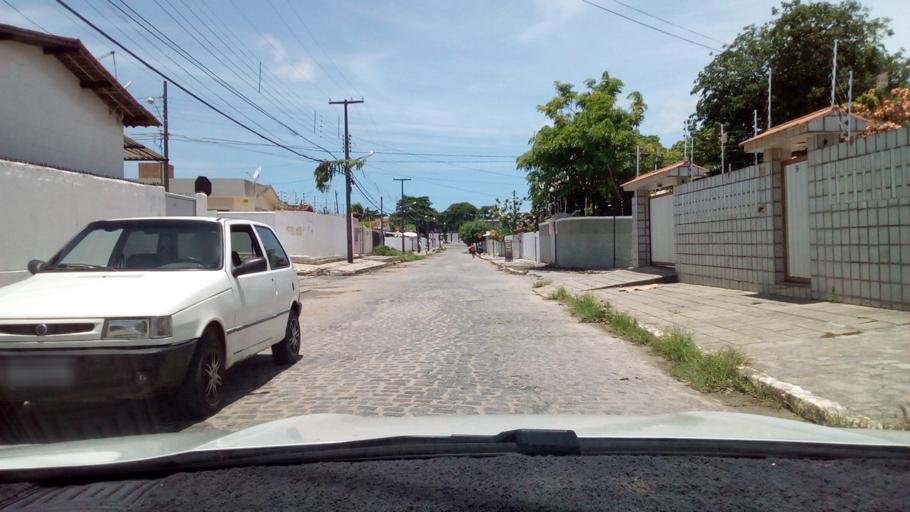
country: BR
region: Paraiba
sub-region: Joao Pessoa
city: Joao Pessoa
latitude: -7.1680
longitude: -34.8678
